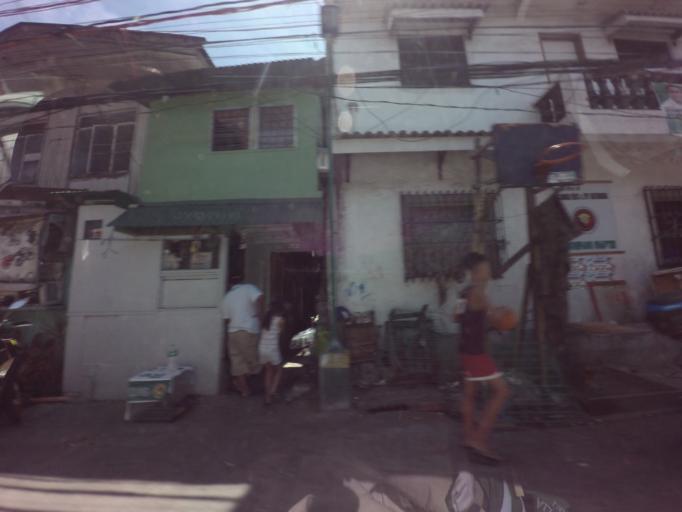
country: PH
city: Sambayanihan People's Village
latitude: 14.4971
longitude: 120.9909
